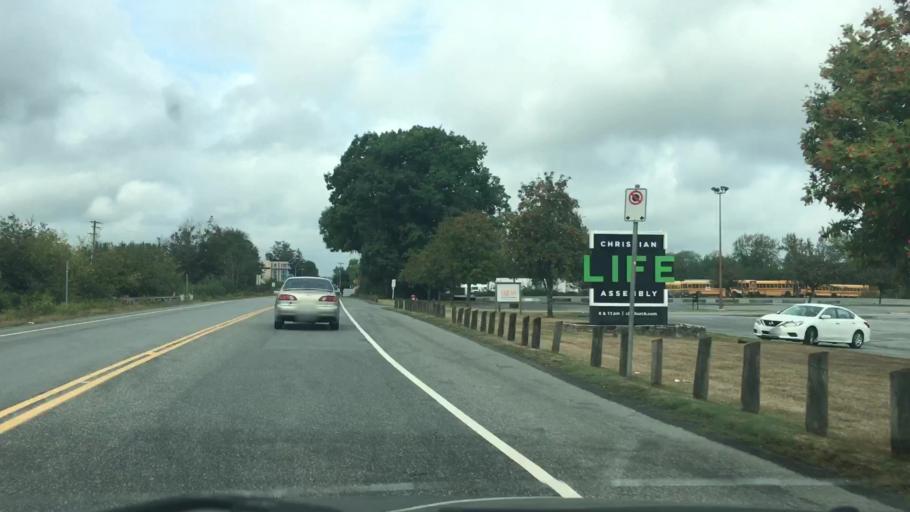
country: CA
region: British Columbia
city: Langley
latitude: 49.1045
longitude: -122.6335
